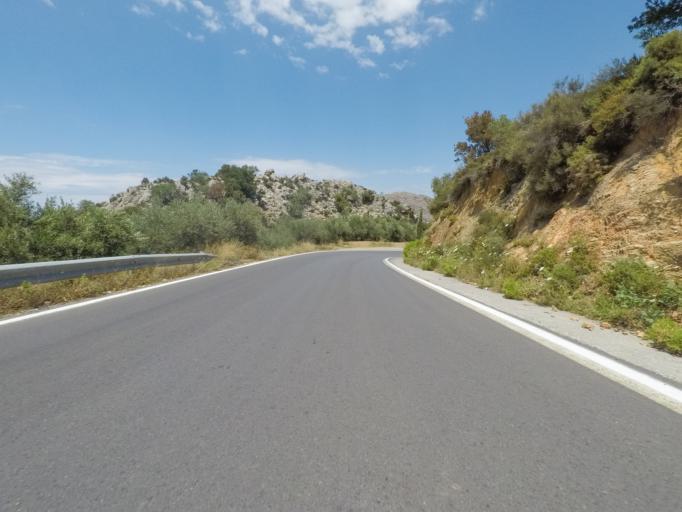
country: GR
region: Crete
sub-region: Nomos Irakleiou
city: Mokhos
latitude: 35.2303
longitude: 25.4591
